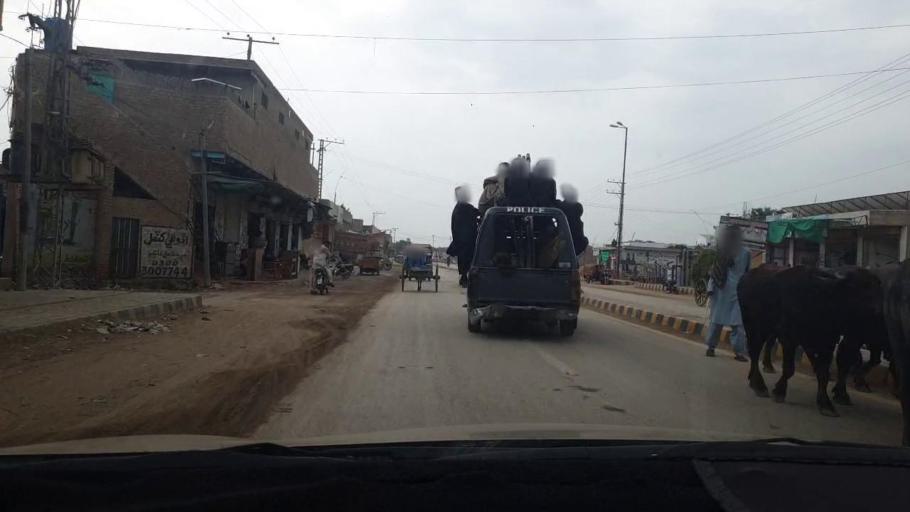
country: PK
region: Sindh
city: Larkana
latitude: 27.5760
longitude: 68.2271
